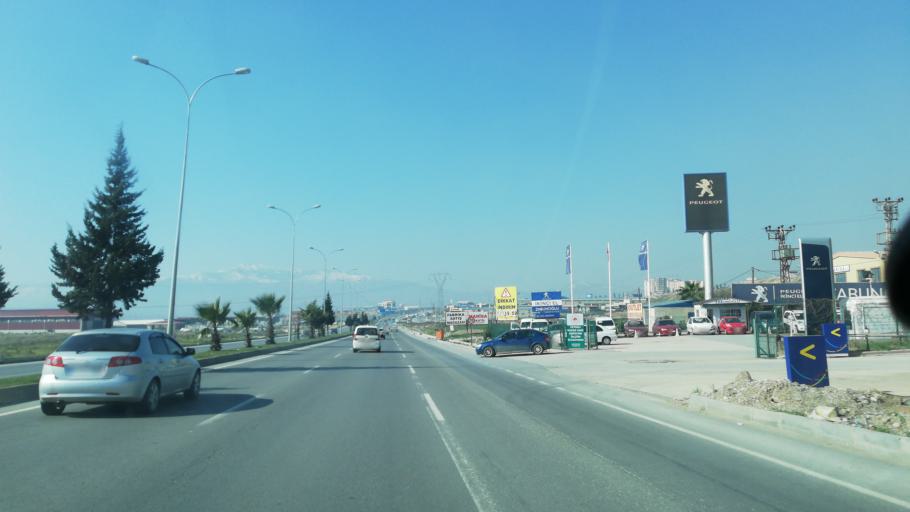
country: TR
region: Kahramanmaras
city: Kahramanmaras
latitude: 37.5652
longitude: 36.8998
